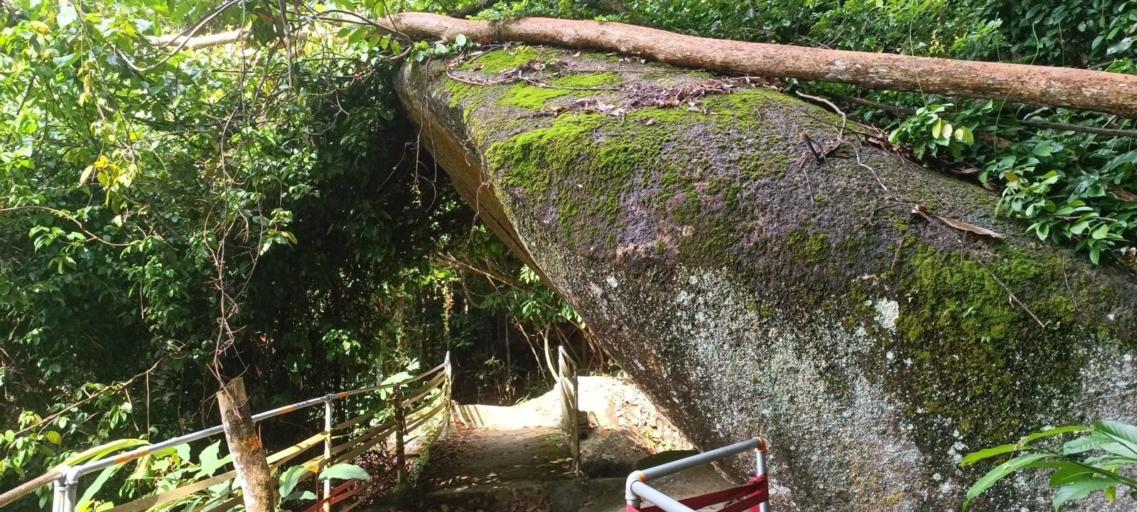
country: MY
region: Penang
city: Tanjung Tokong
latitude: 5.4231
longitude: 100.2861
